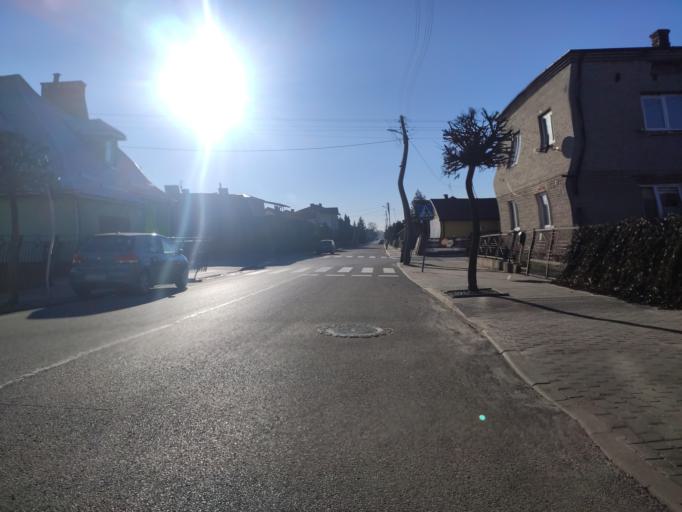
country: PL
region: Lublin Voivodeship
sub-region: Powiat lubartowski
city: Kock
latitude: 51.6394
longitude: 22.4450
